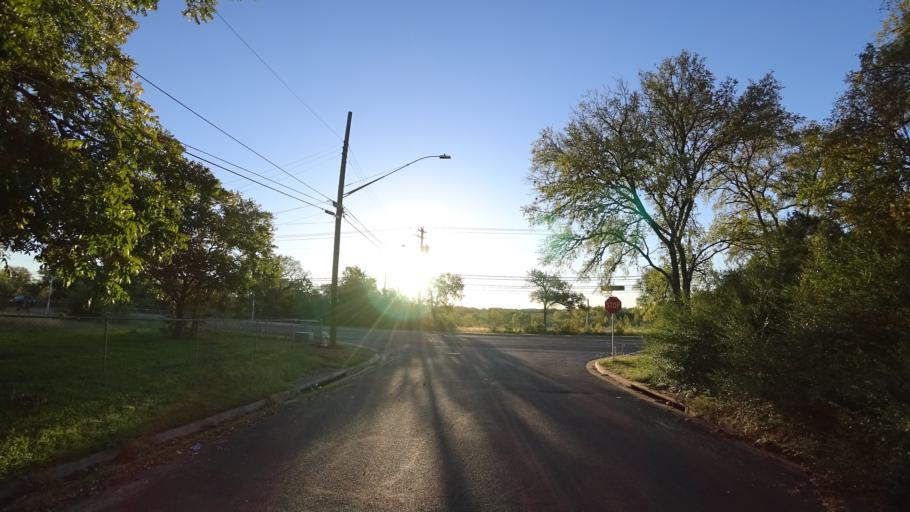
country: US
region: Texas
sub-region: Travis County
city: Austin
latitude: 30.2894
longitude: -97.6806
